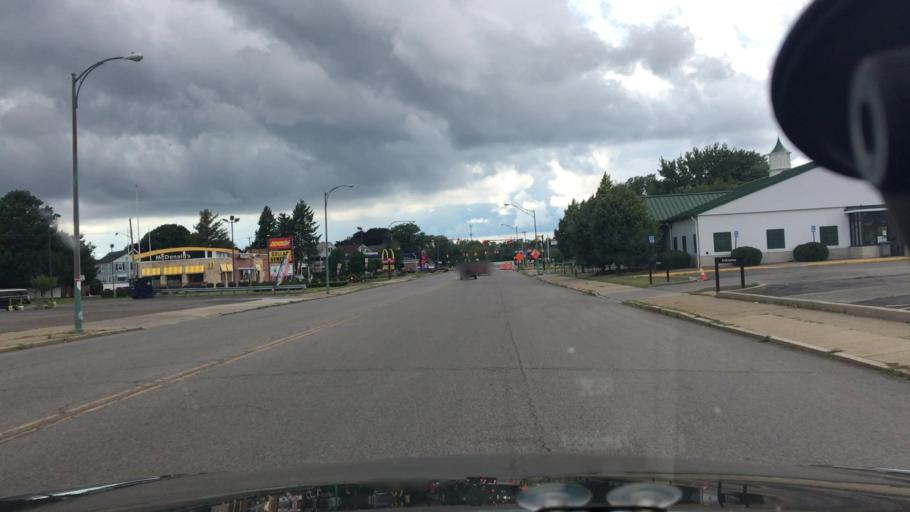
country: US
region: New York
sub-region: Erie County
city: West Seneca
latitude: 42.8569
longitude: -78.8239
